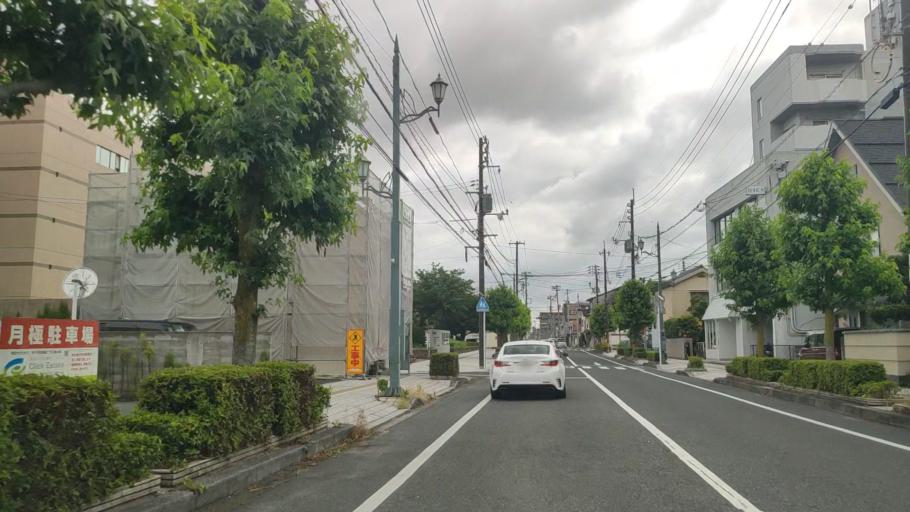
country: JP
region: Tottori
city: Yonago
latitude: 35.4269
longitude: 133.3327
